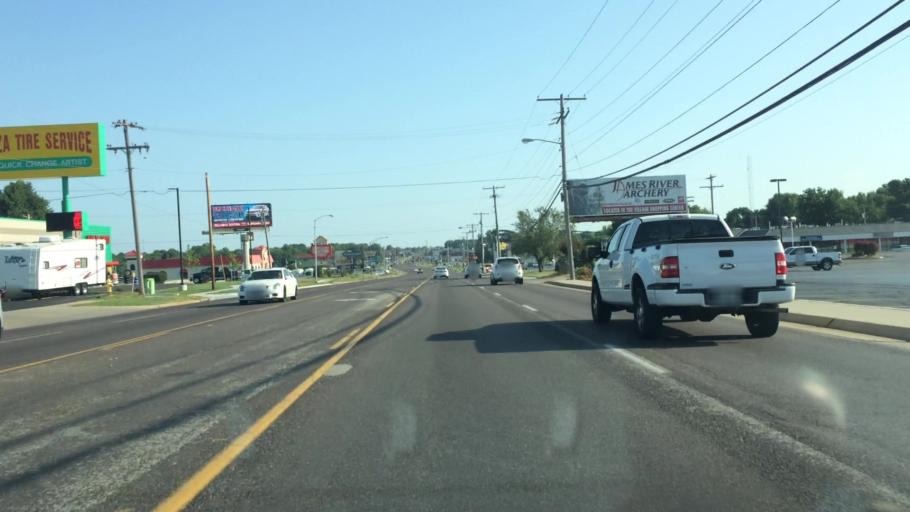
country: US
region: Missouri
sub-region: Greene County
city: Springfield
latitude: 37.1620
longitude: -93.2954
